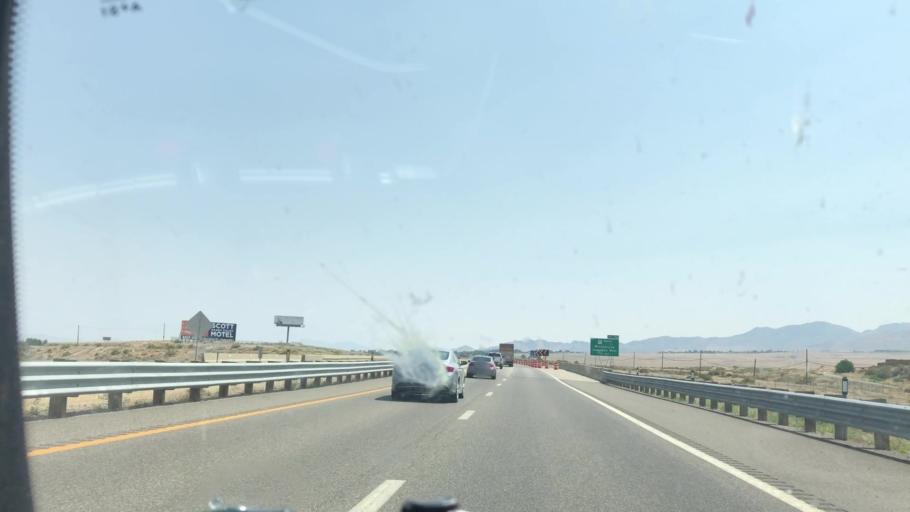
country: US
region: Nevada
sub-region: Humboldt County
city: Winnemucca
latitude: 40.9447
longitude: -117.7670
